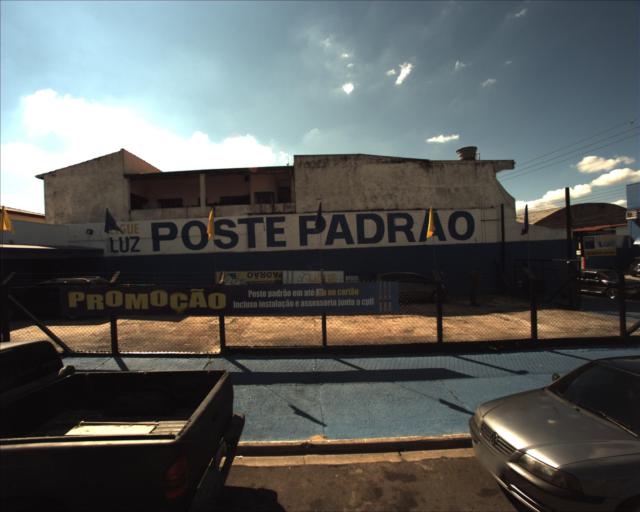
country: BR
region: Sao Paulo
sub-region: Sorocaba
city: Sorocaba
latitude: -23.4756
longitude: -47.4722
